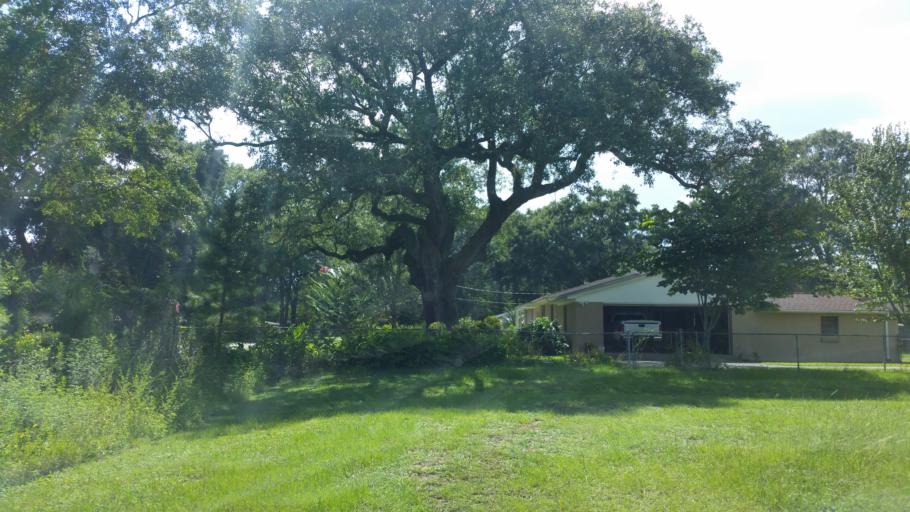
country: US
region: Florida
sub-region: Escambia County
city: Ensley
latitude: 30.5289
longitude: -87.2581
